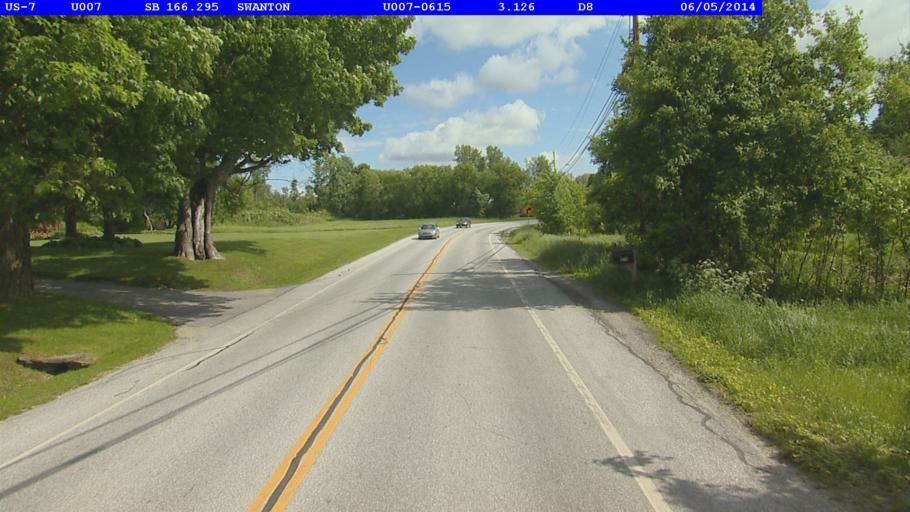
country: US
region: Vermont
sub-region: Franklin County
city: Swanton
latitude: 44.8912
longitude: -73.0907
